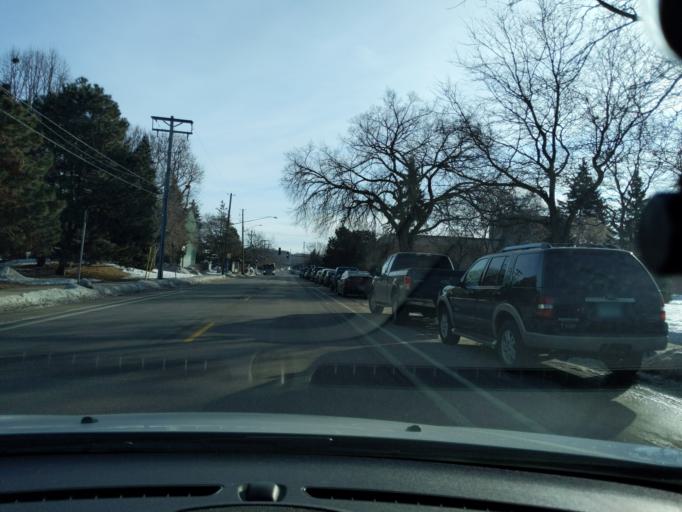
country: US
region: Minnesota
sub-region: Ramsey County
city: Lauderdale
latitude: 44.9880
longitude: -93.2147
